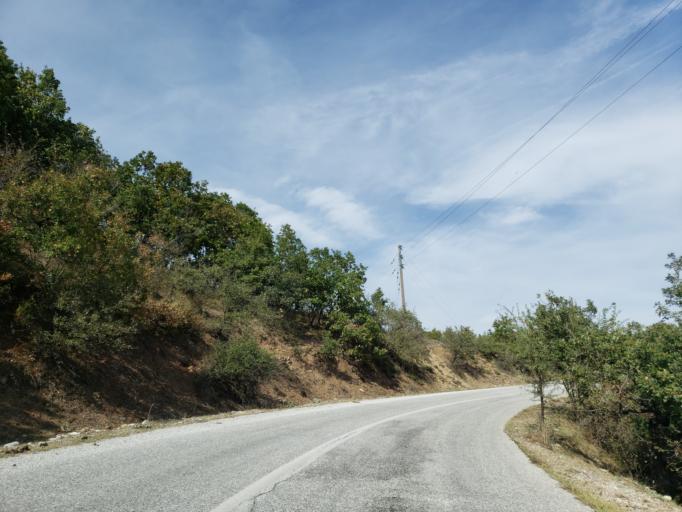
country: GR
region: Thessaly
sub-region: Trikala
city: Kastraki
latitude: 39.7386
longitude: 21.6552
